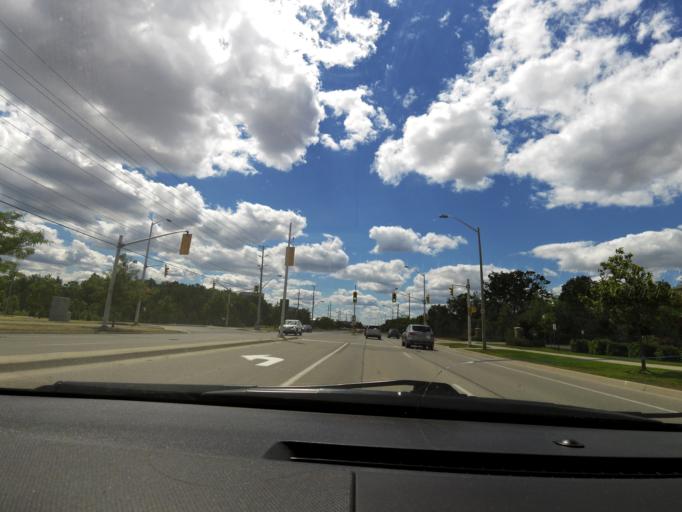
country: CA
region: Ontario
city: Burlington
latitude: 43.3980
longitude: -79.7862
